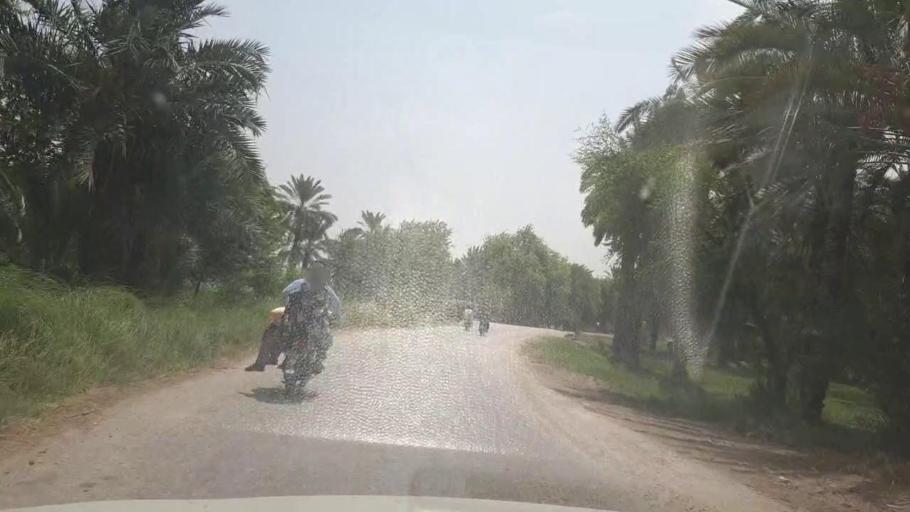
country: PK
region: Sindh
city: Kot Diji
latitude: 27.3728
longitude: 68.7193
